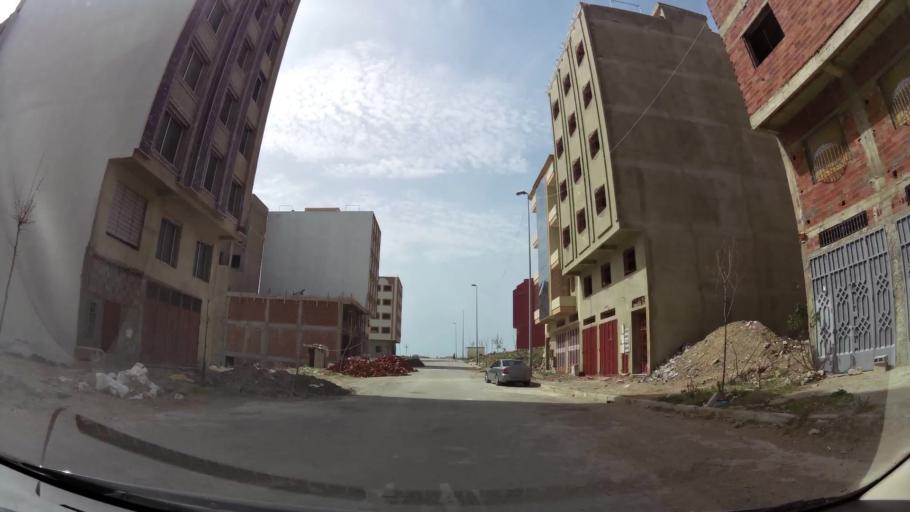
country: MA
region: Tanger-Tetouan
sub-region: Tanger-Assilah
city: Tangier
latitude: 35.7387
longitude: -5.8371
